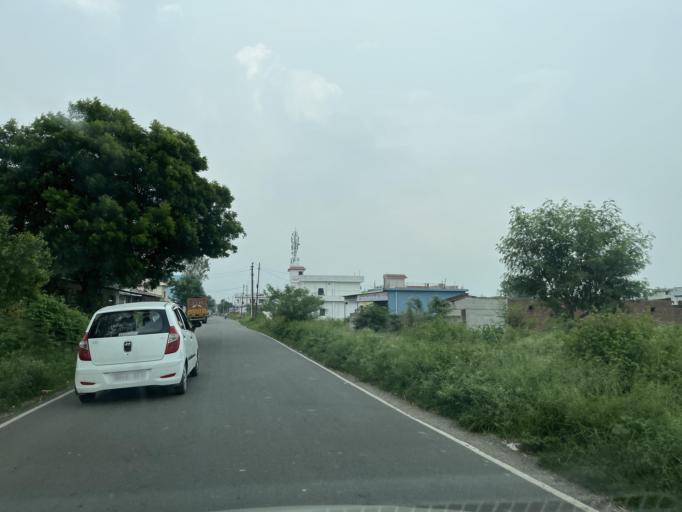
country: IN
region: Uttarakhand
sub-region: Naini Tal
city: Haldwani
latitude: 29.1936
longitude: 79.4832
